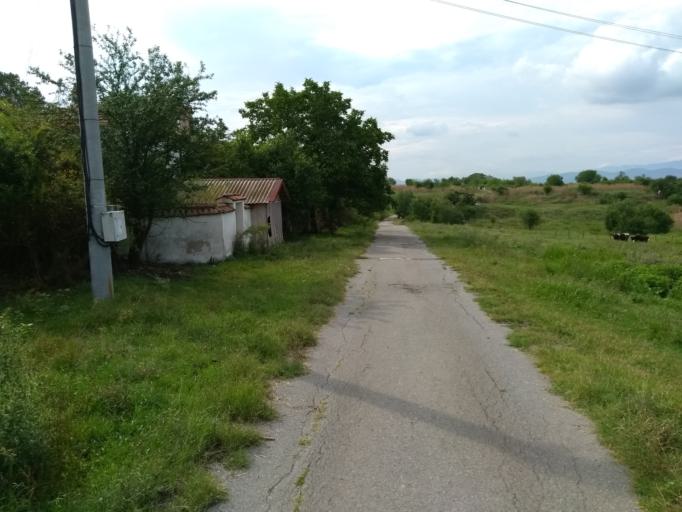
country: BG
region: Sliven
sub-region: Obshtina Sliven
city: Kermen
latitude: 42.4603
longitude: 26.1389
